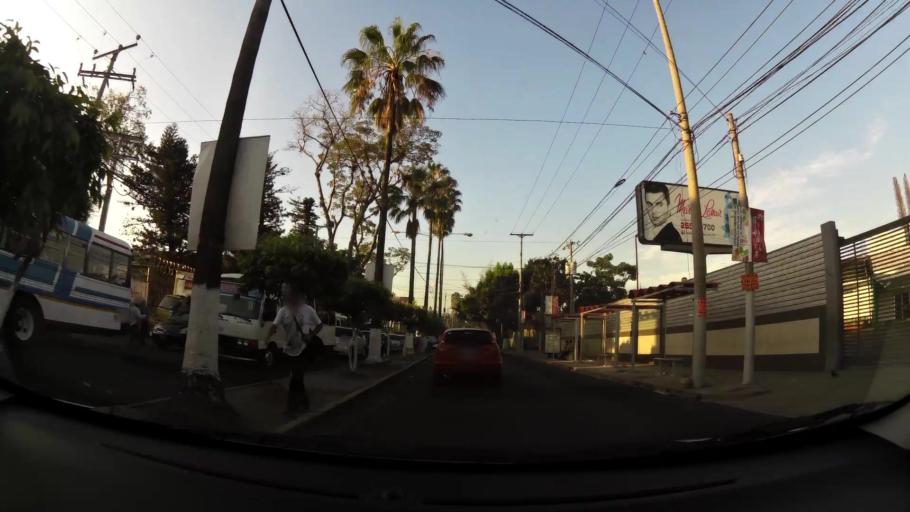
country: SV
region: La Libertad
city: Antiguo Cuscatlan
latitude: 13.6931
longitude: -89.2299
